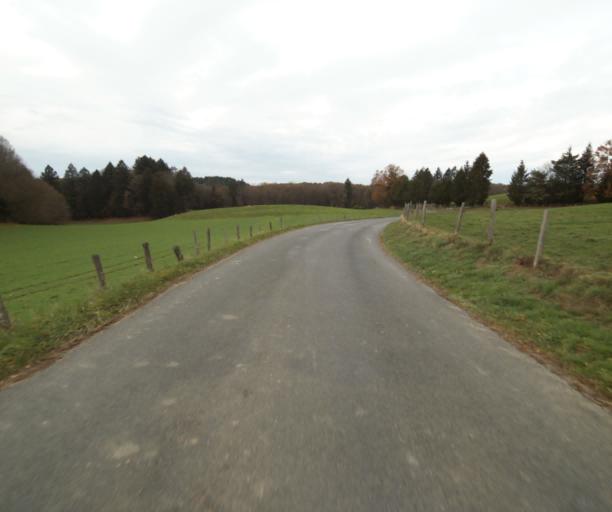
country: FR
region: Limousin
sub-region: Departement de la Correze
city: Chameyrat
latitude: 45.2565
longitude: 1.6796
